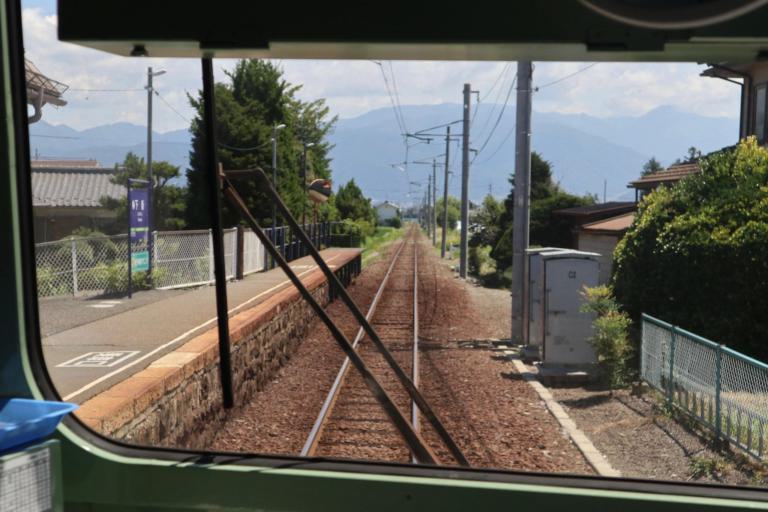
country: JP
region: Nagano
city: Matsumoto
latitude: 36.2251
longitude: 137.9222
